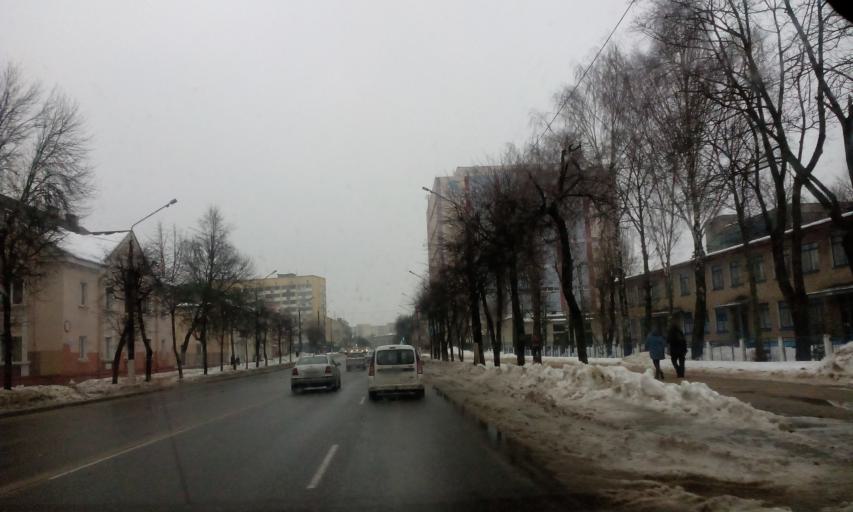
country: BY
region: Mogilev
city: Mahilyow
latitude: 53.8994
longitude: 30.3407
